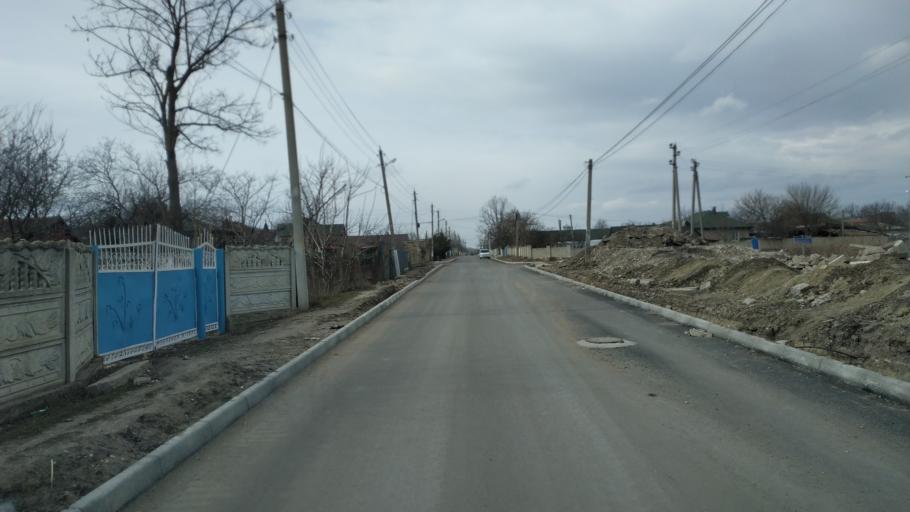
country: MD
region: Laloveni
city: Ialoveni
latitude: 46.8594
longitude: 28.7864
